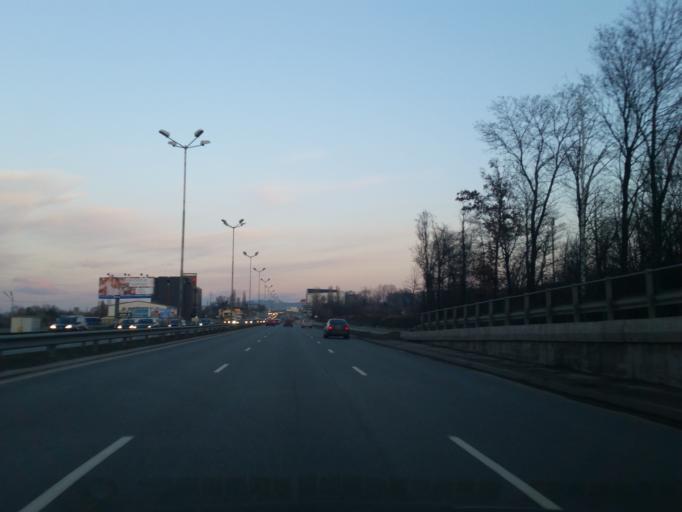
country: BG
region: Sofia-Capital
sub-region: Stolichna Obshtina
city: Sofia
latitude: 42.6464
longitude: 23.3007
